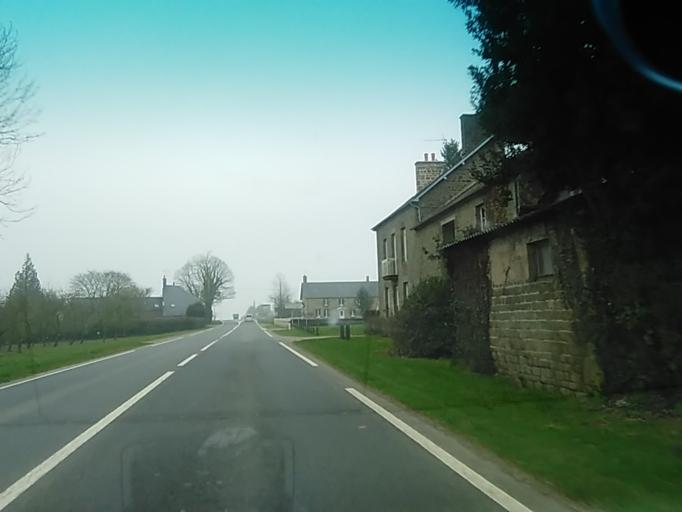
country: FR
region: Lower Normandy
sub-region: Departement de l'Orne
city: Magny-le-Desert
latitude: 48.6101
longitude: -0.3170
